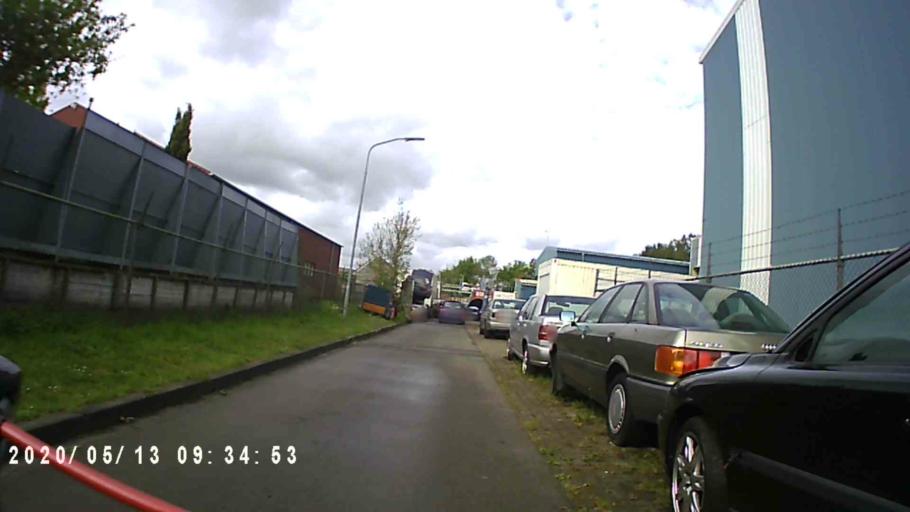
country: NL
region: Groningen
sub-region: Gemeente Zuidhorn
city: Noordhorn
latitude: 53.2548
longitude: 6.3897
